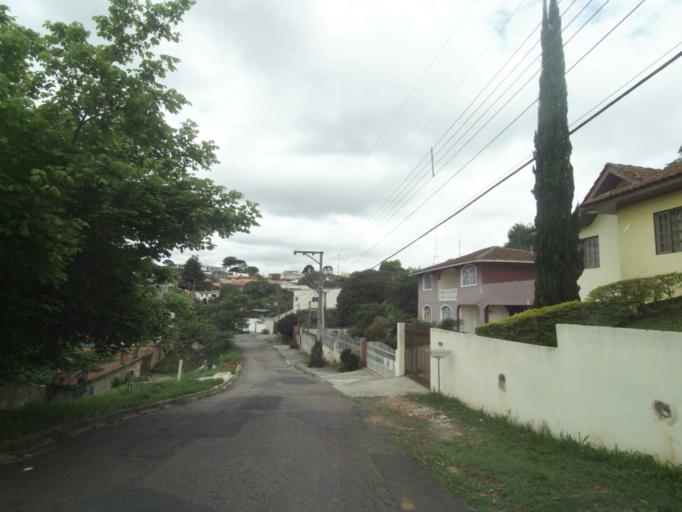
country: BR
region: Parana
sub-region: Curitiba
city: Curitiba
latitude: -25.3900
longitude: -49.2869
